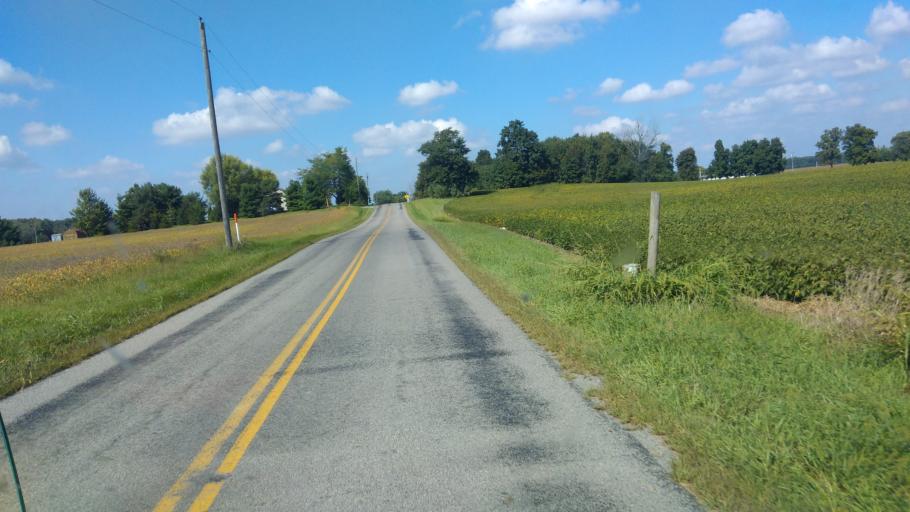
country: US
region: Ohio
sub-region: Logan County
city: Lakeview
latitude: 40.6198
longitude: -83.8804
